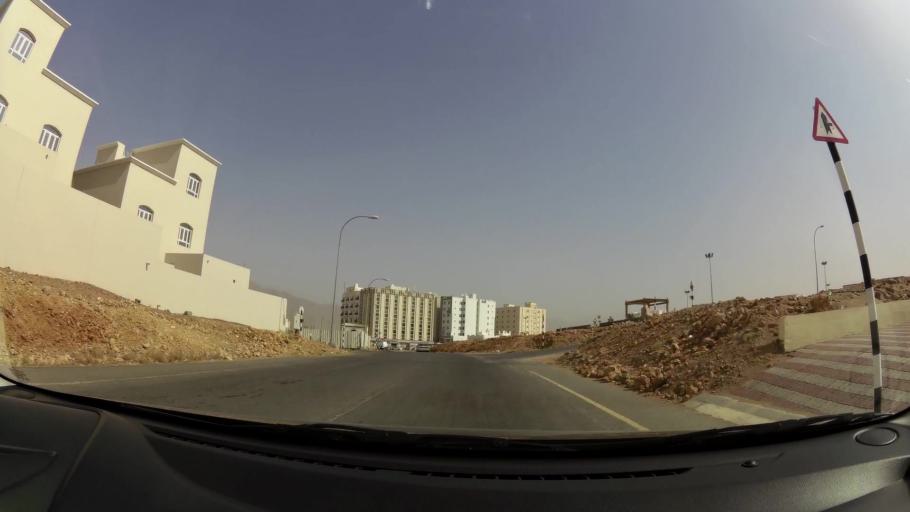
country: OM
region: Muhafazat Masqat
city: Bawshar
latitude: 23.5538
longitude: 58.3458
